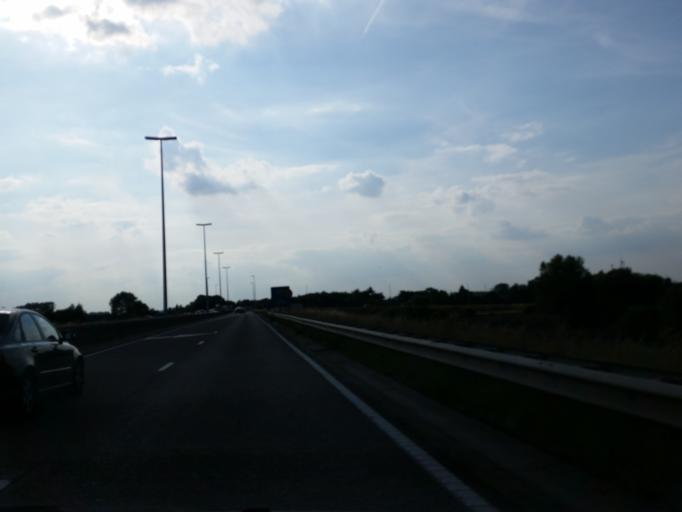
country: BE
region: Flanders
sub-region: Provincie Antwerpen
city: Willebroek
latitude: 51.0481
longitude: 4.3391
